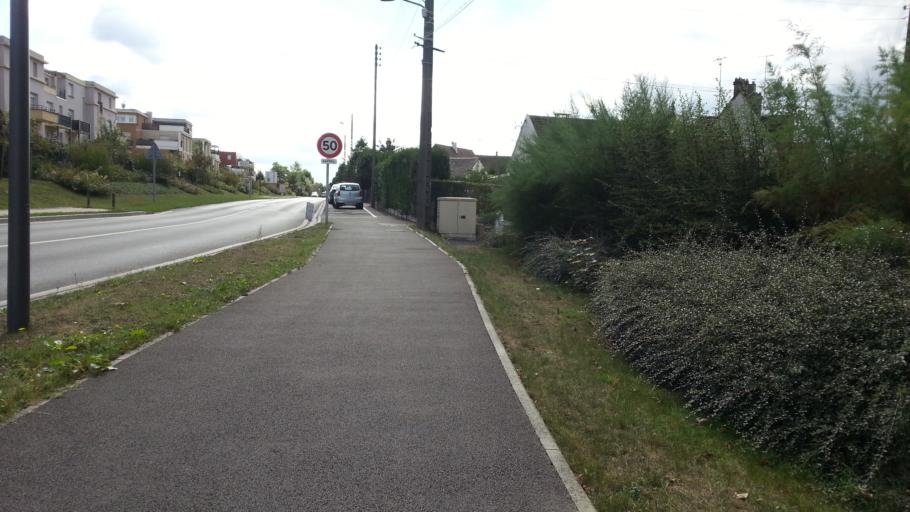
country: FR
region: Picardie
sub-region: Departement de l'Oise
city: Saint-Maximin
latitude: 49.2244
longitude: 2.4558
